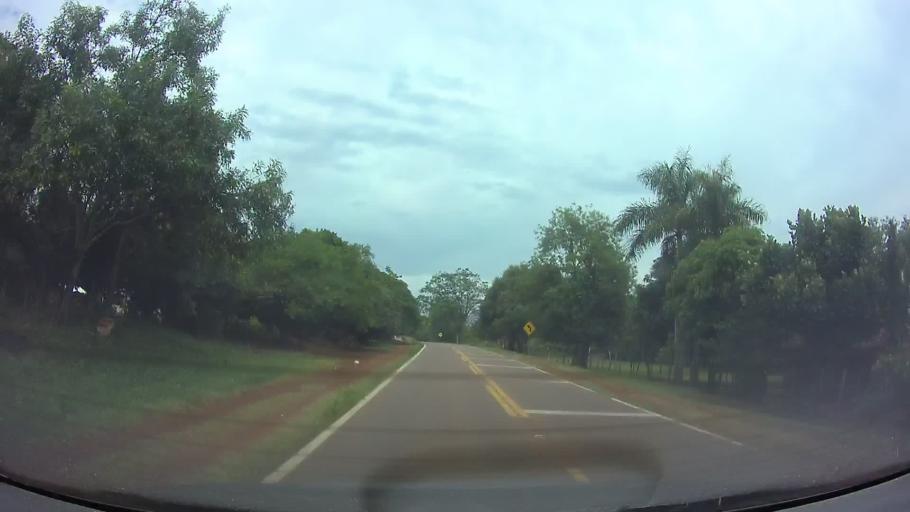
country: PY
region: Paraguari
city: Acahay
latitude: -25.8606
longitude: -57.1324
